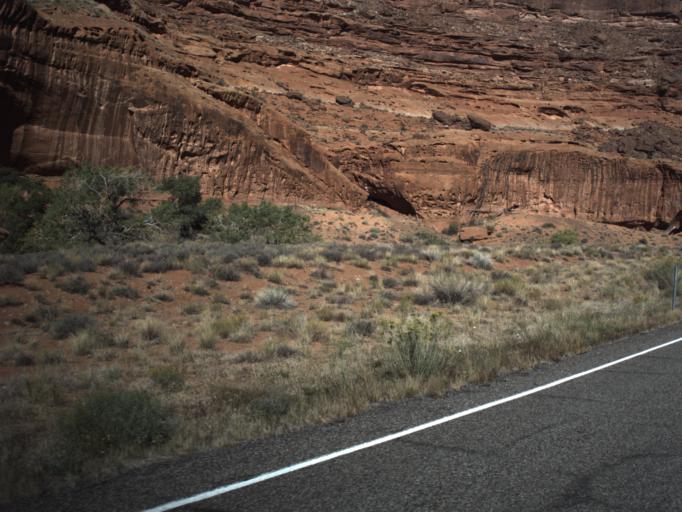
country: US
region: Utah
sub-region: San Juan County
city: Blanding
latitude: 37.9683
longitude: -110.4915
